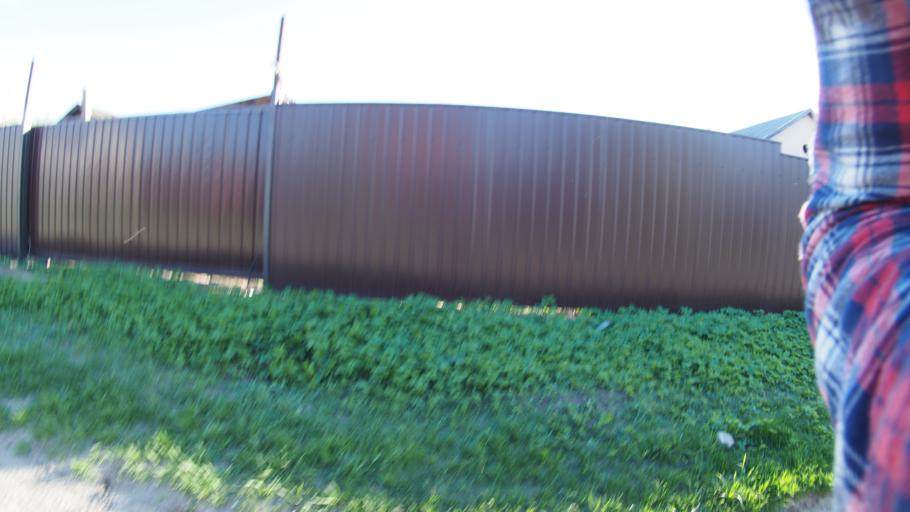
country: RU
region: Moskovskaya
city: Ramenskoye
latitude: 55.5587
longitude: 38.2105
